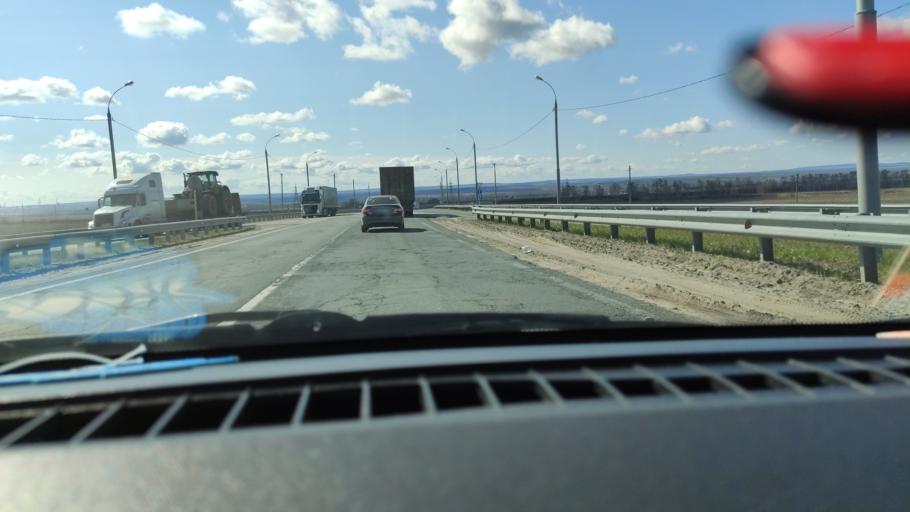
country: RU
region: Samara
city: Varlamovo
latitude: 53.1904
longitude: 48.2920
